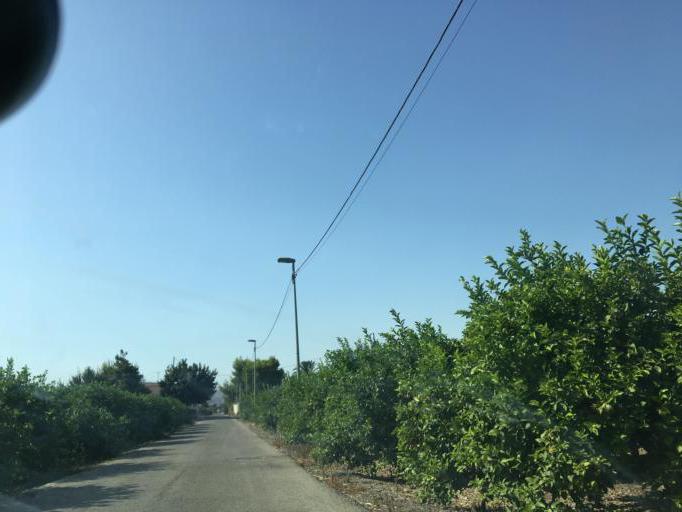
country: ES
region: Murcia
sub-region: Murcia
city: Santomera
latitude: 38.0263
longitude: -1.0544
